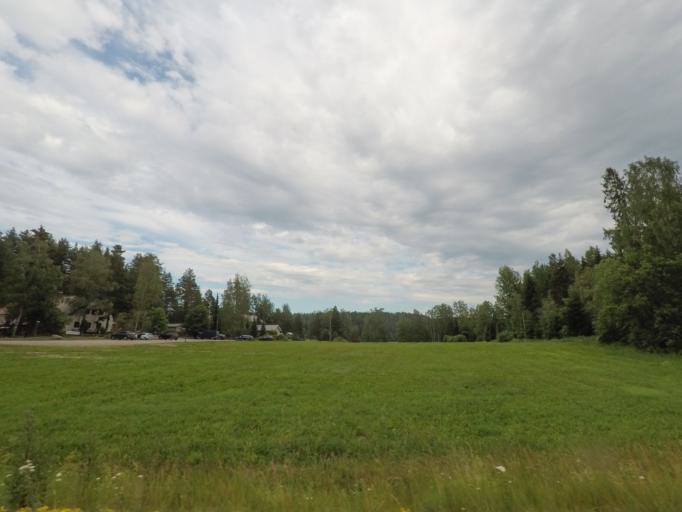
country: FI
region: Uusimaa
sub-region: Helsinki
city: Maentsaelae
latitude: 60.7473
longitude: 25.4320
